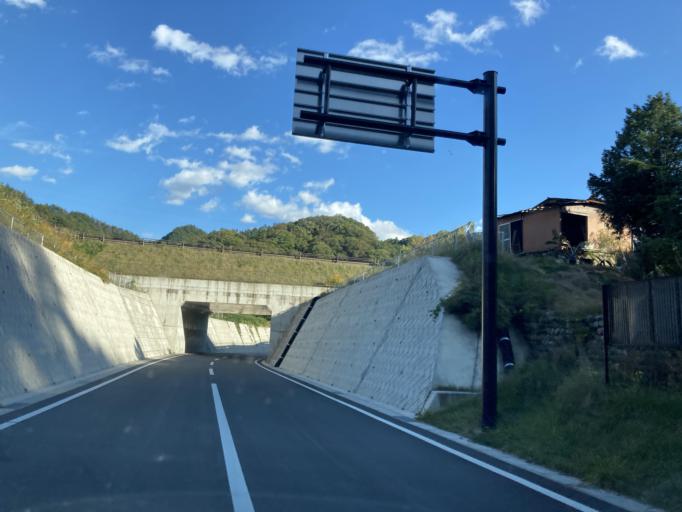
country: JP
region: Nagano
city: Omachi
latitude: 36.4661
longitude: 137.9588
